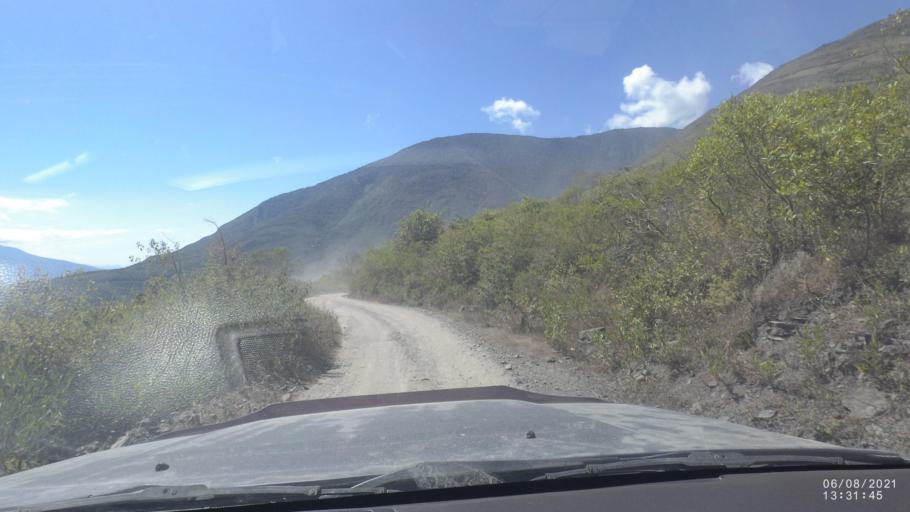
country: BO
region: La Paz
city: Quime
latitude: -16.7013
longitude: -66.7280
